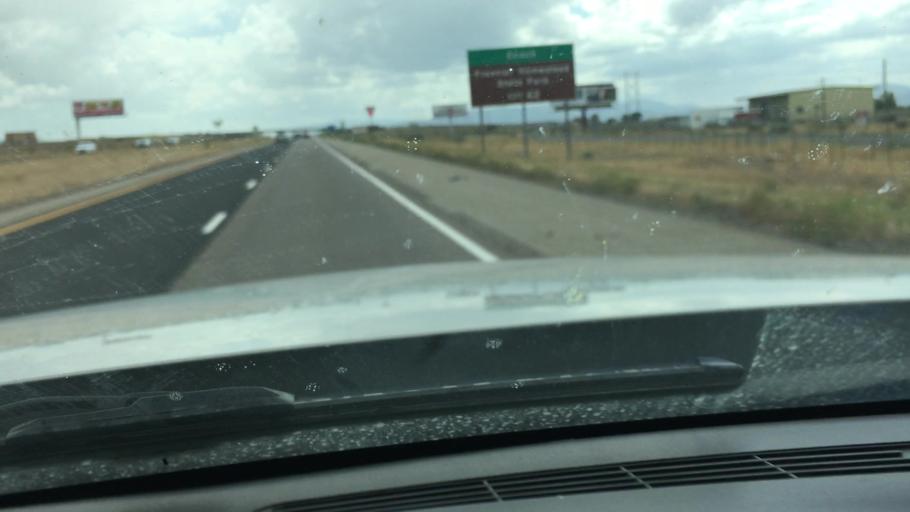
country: US
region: Utah
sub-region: Iron County
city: Enoch
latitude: 37.7367
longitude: -113.0443
